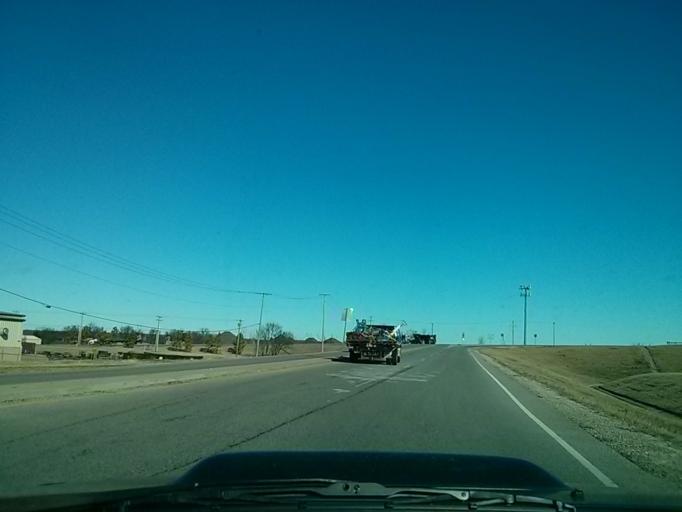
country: US
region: Oklahoma
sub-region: Tulsa County
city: Glenpool
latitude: 36.0012
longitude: -96.0136
